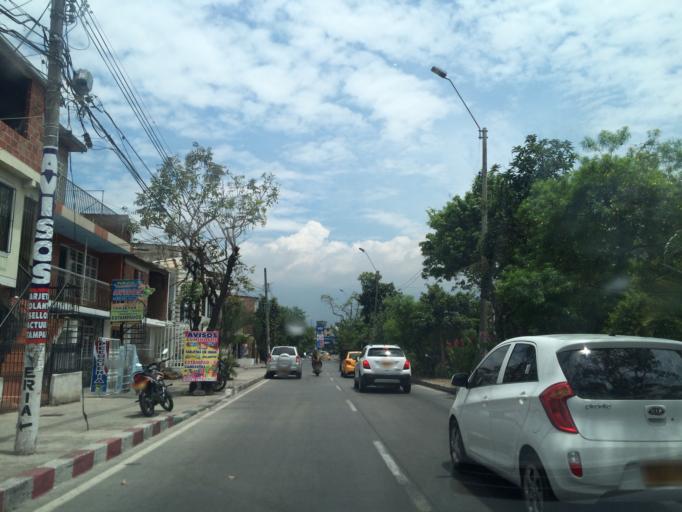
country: CO
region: Valle del Cauca
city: Cali
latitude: 3.4183
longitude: -76.5257
